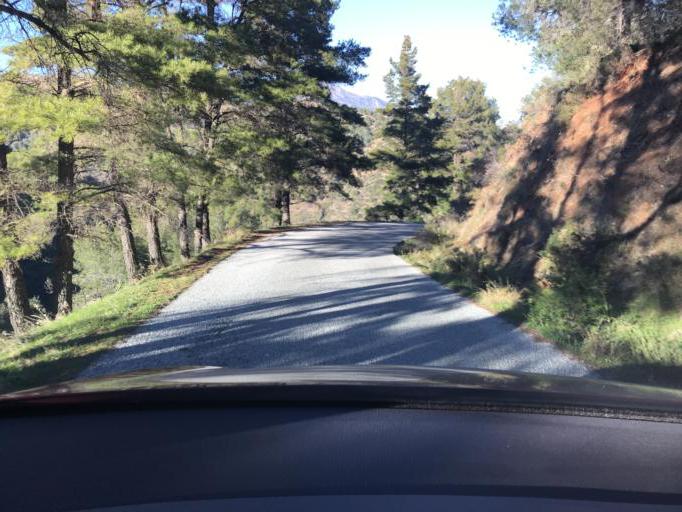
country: ES
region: Andalusia
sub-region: Provincia de Malaga
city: Tolox
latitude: 36.6836
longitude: -4.9138
